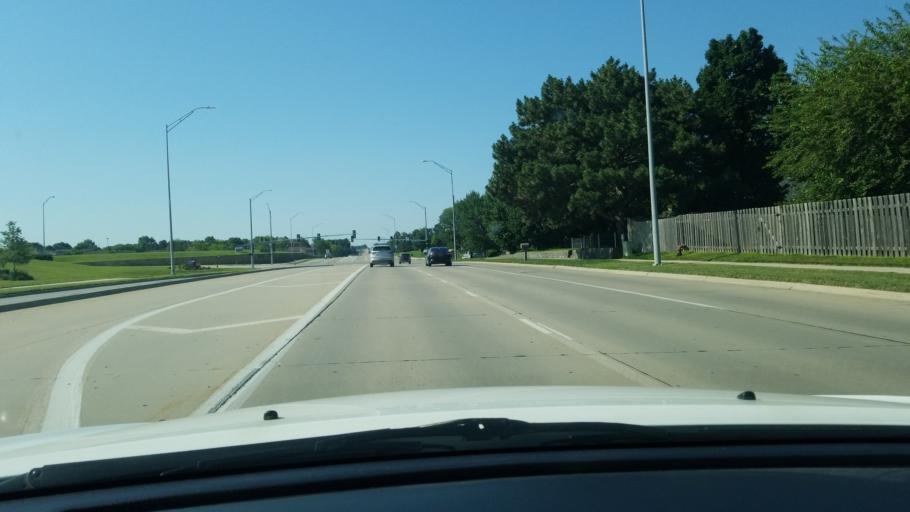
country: US
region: Nebraska
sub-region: Lancaster County
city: Lincoln
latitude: 40.7713
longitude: -96.6062
